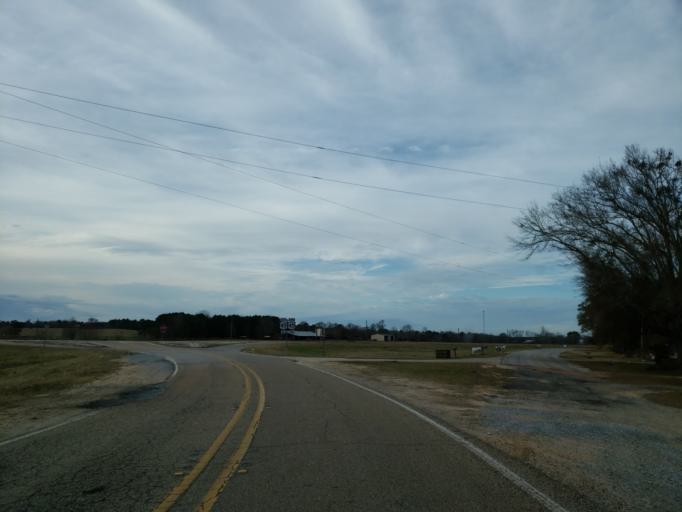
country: US
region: Mississippi
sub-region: Clarke County
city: Quitman
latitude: 31.8794
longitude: -88.7111
